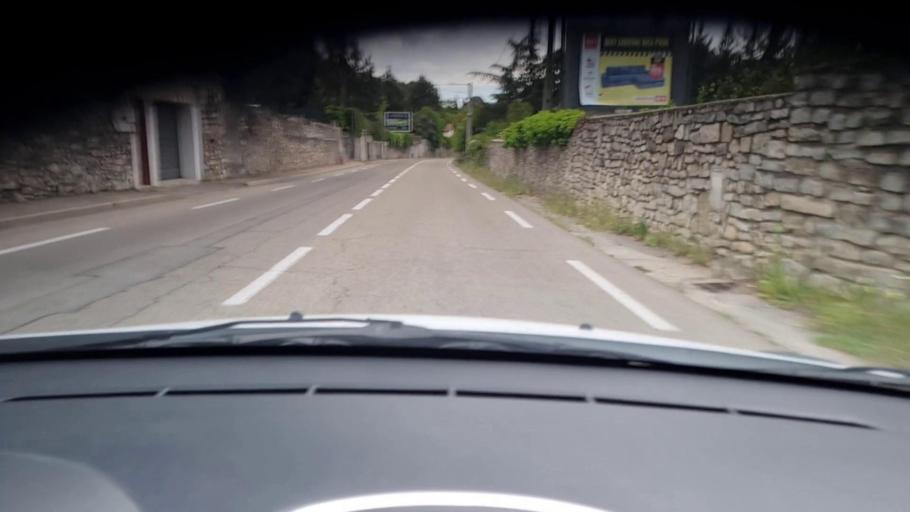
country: FR
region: Languedoc-Roussillon
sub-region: Departement du Gard
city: Nimes
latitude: 43.8609
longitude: 4.3772
